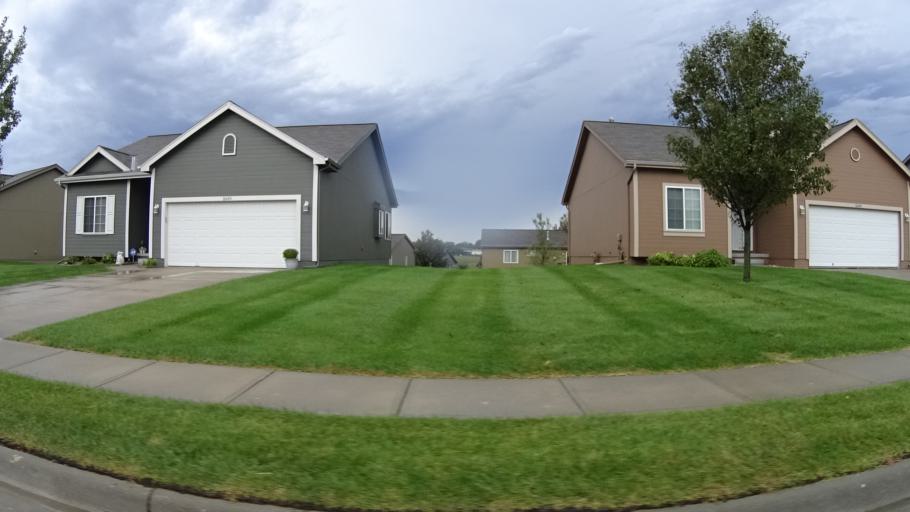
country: US
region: Nebraska
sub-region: Sarpy County
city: Offutt Air Force Base
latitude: 41.1550
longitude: -95.9484
